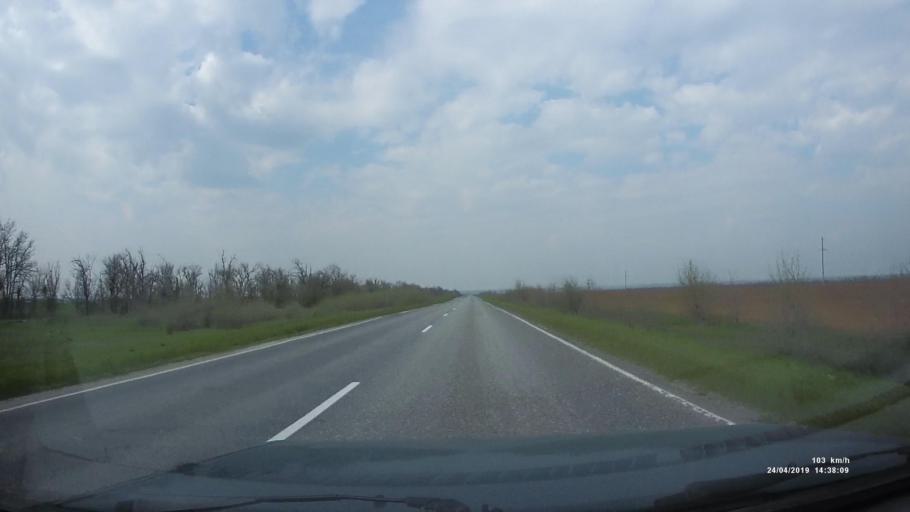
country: RU
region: Rostov
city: Remontnoye
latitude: 46.3963
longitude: 43.8861
